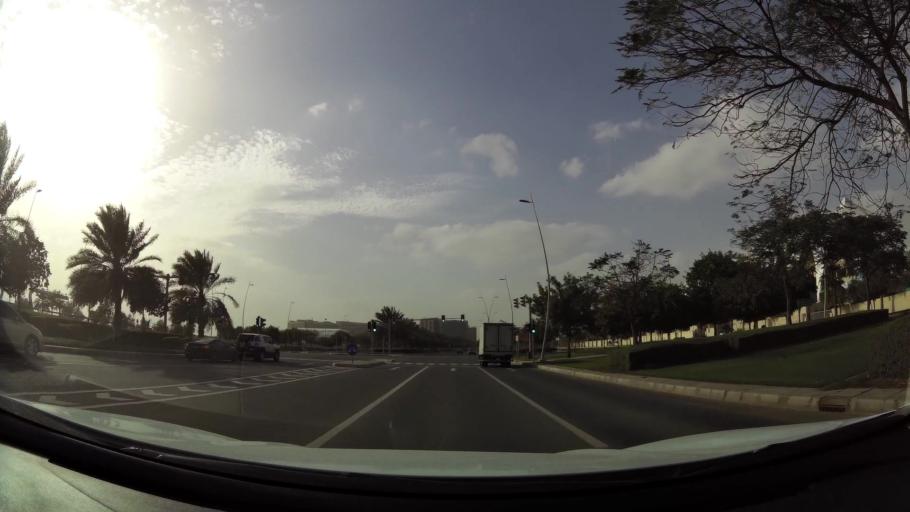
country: AE
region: Abu Dhabi
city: Abu Dhabi
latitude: 24.4635
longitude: 54.6052
